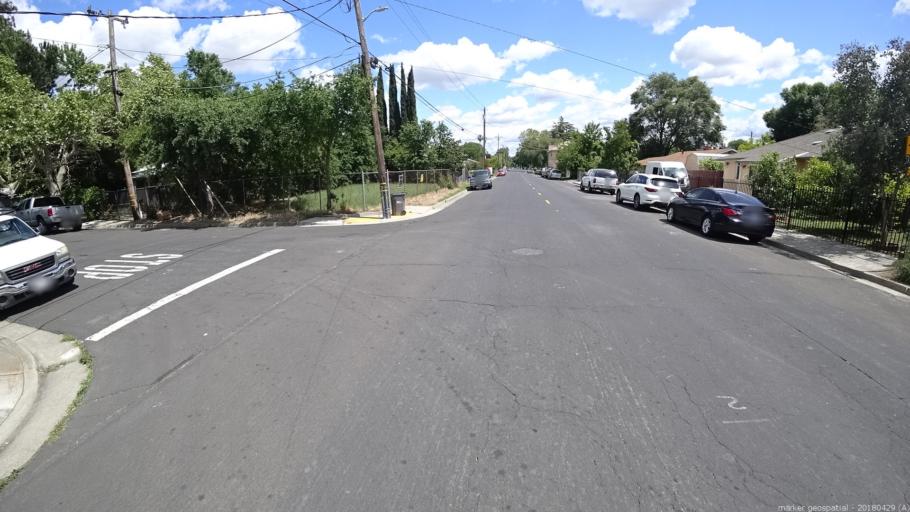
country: US
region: California
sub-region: Yolo County
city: West Sacramento
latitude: 38.5943
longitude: -121.5437
